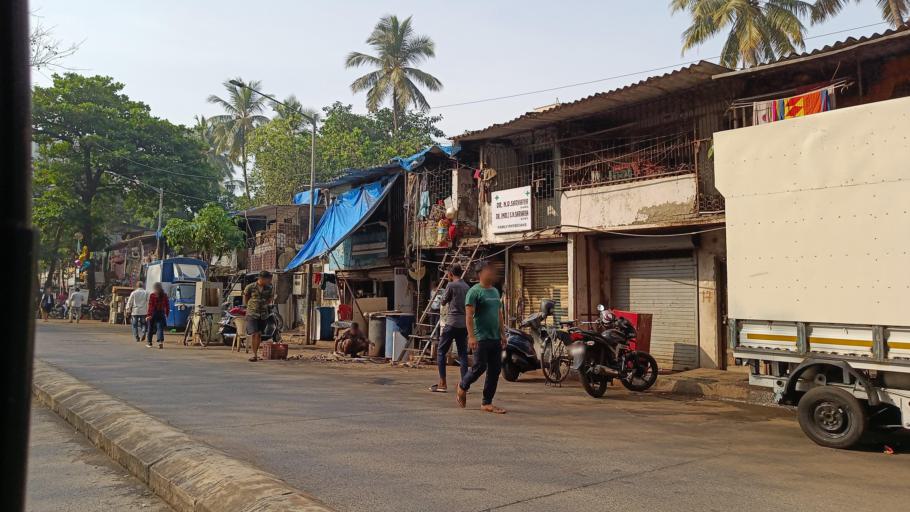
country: IN
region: Maharashtra
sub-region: Mumbai Suburban
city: Mumbai
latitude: 19.1257
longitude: 72.8288
